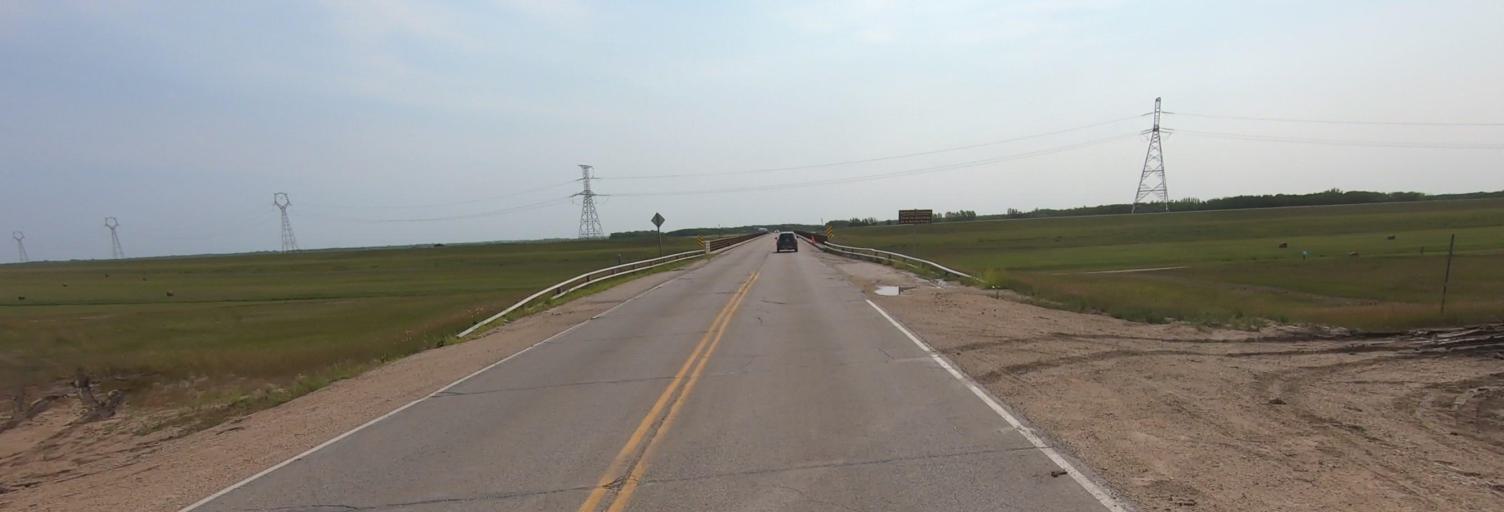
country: CA
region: Manitoba
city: Winnipeg
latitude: 49.7573
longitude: -97.1237
